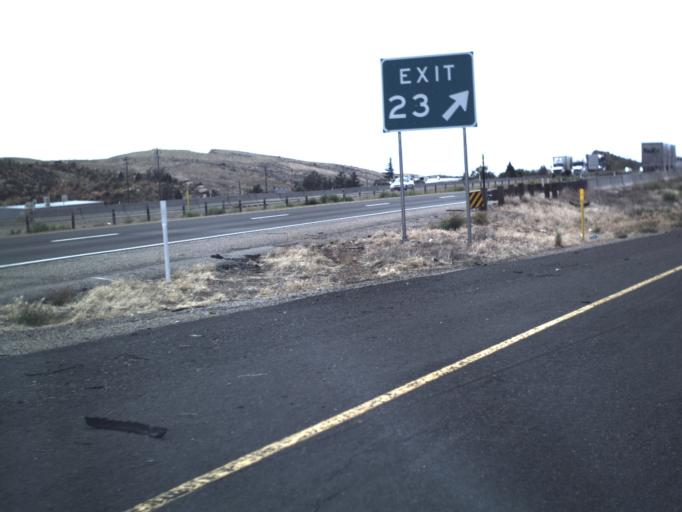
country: US
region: Utah
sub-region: Washington County
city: Toquerville
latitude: 37.2458
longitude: -113.3511
